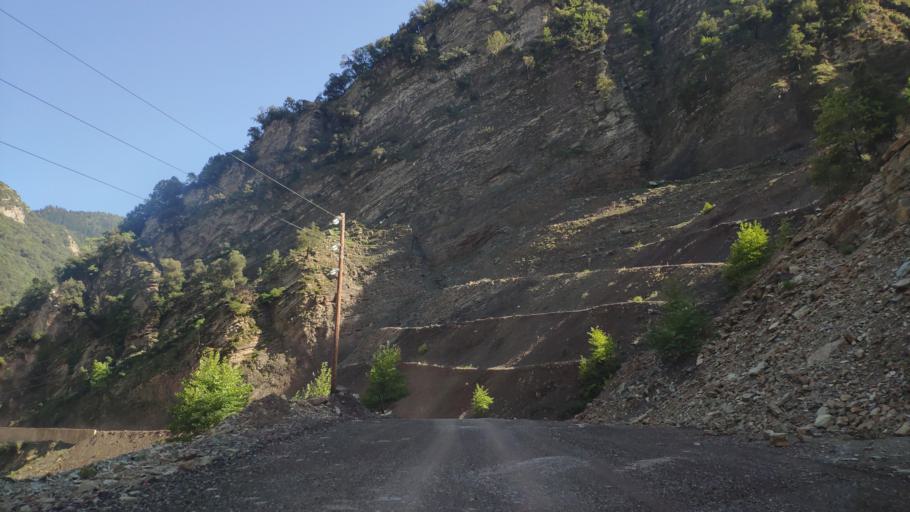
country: GR
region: Central Greece
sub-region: Nomos Evrytanias
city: Kerasochori
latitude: 39.0717
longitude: 21.6014
